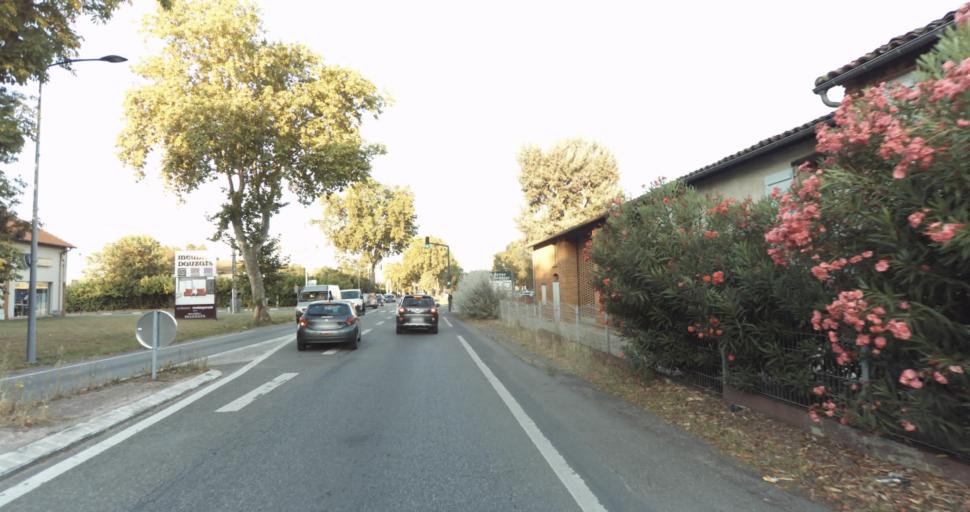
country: FR
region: Midi-Pyrenees
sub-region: Departement de la Haute-Garonne
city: L'Union
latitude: 43.6595
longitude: 1.4877
